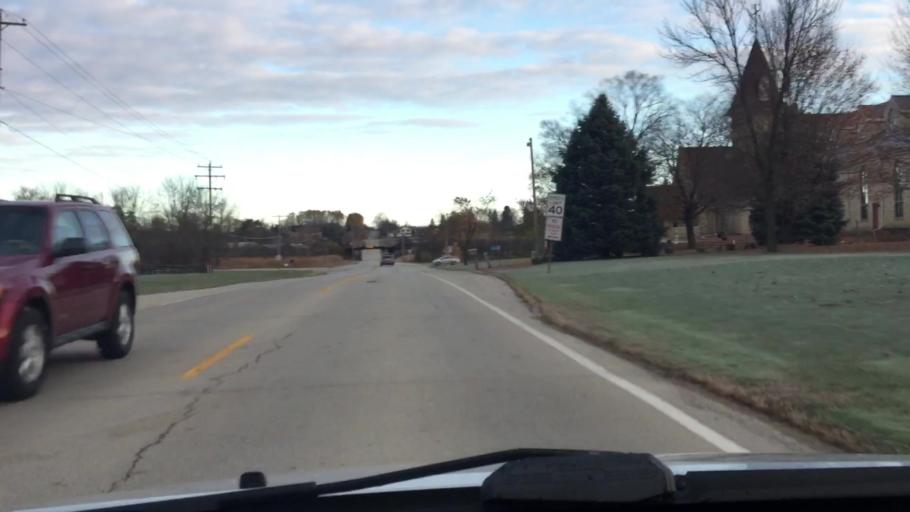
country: US
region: Wisconsin
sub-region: Waukesha County
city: Okauchee Lake
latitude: 43.1742
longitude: -88.4590
